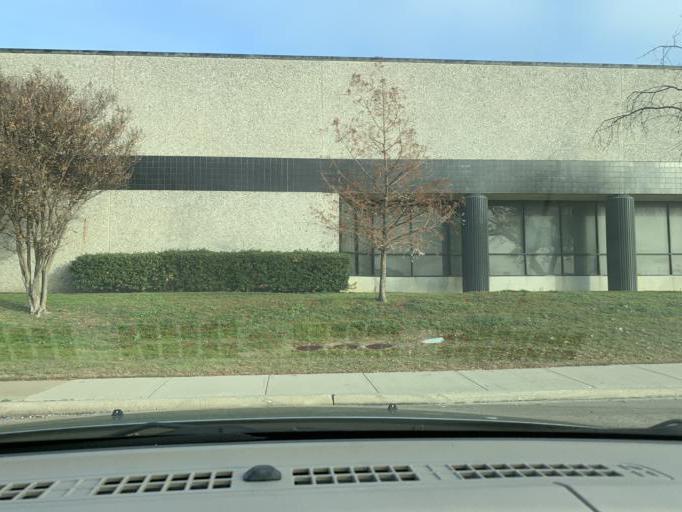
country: US
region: Texas
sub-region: Dallas County
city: Carrollton
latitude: 32.9589
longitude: -96.9200
